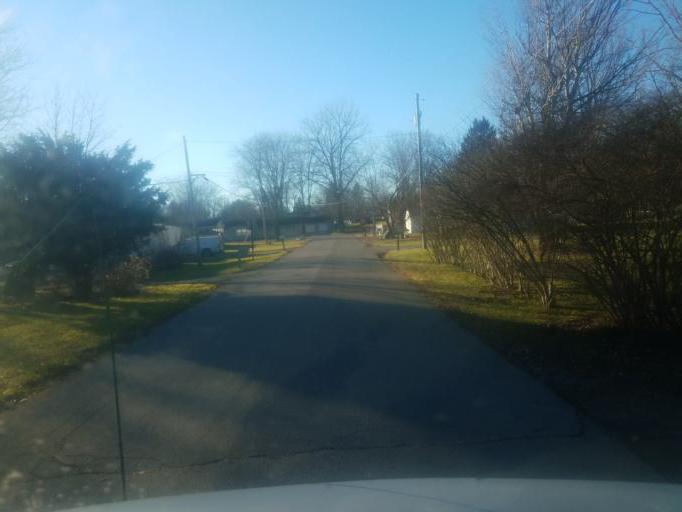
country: US
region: Ohio
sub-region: Richland County
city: Mansfield
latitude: 40.7903
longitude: -82.5327
